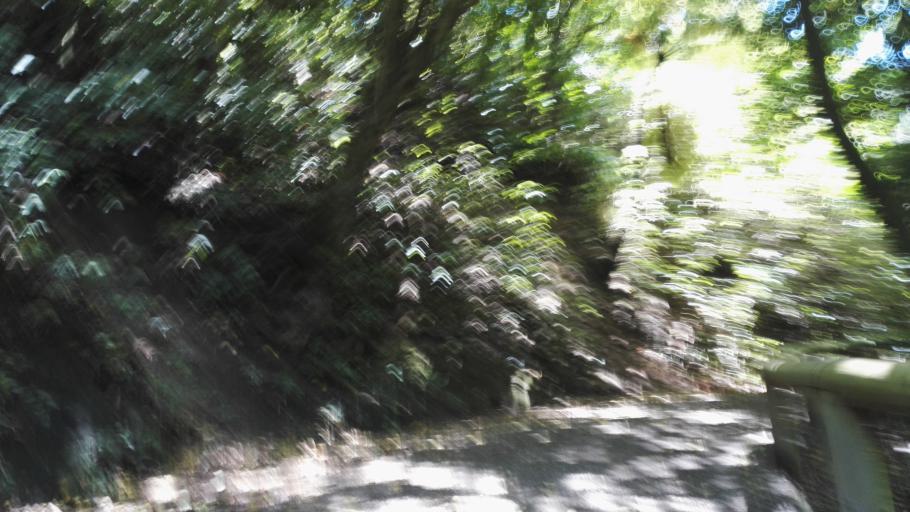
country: NZ
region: Wellington
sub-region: Wellington City
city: Kelburn
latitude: -41.2823
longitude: 174.7688
